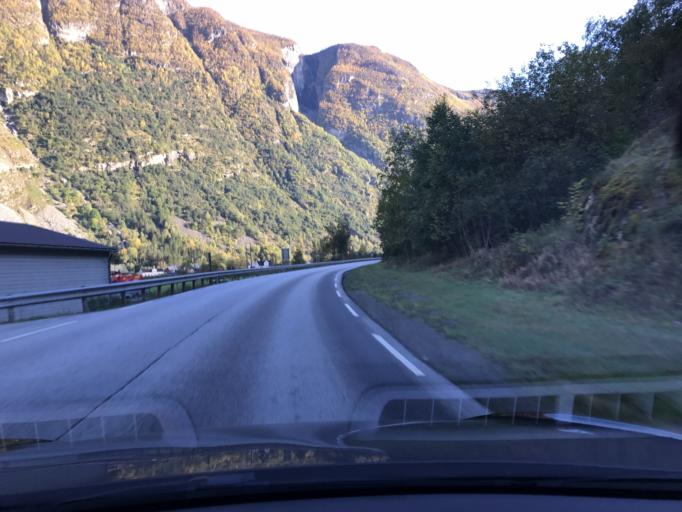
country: NO
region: Sogn og Fjordane
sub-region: Laerdal
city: Laerdalsoyri
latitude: 61.0976
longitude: 7.5165
